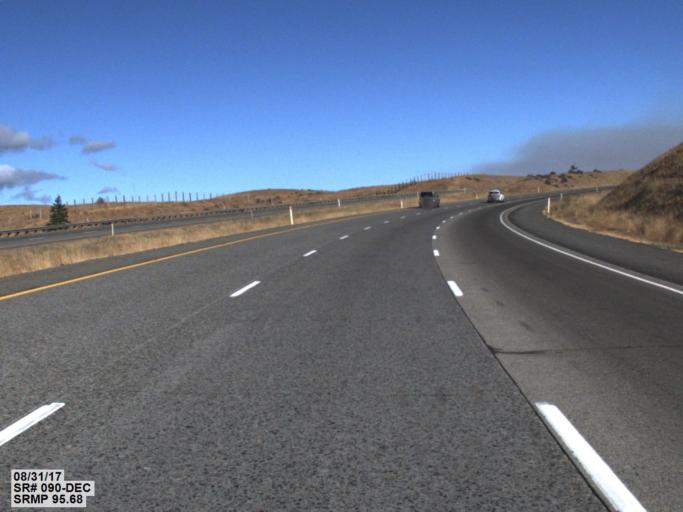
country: US
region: Washington
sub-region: Kittitas County
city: Cle Elum
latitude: 47.0962
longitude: -120.7595
